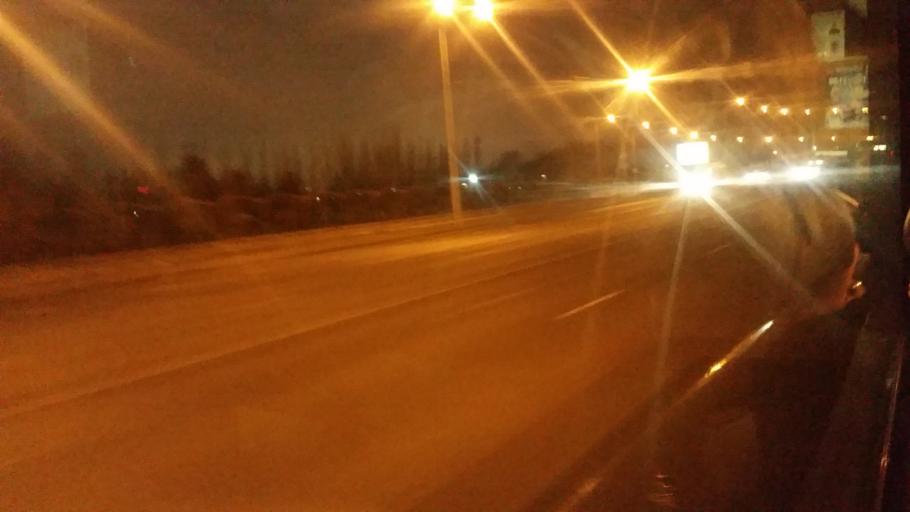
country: KZ
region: Astana Qalasy
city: Astana
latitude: 51.1340
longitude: 71.4412
